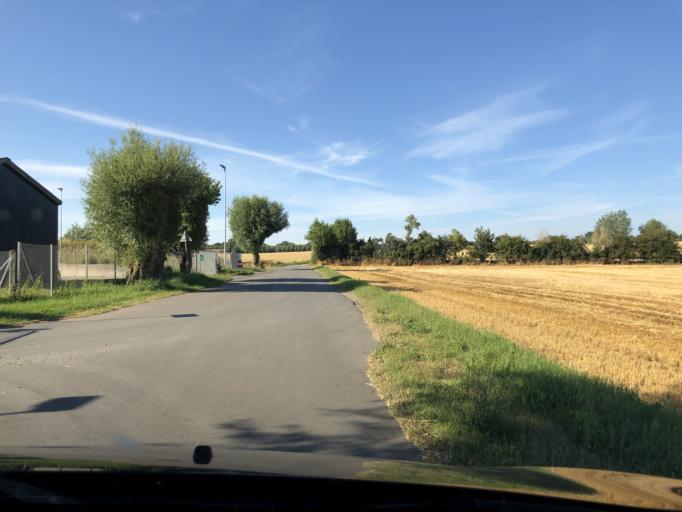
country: DK
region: South Denmark
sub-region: AEro Kommune
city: AEroskobing
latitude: 54.8573
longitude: 10.3643
